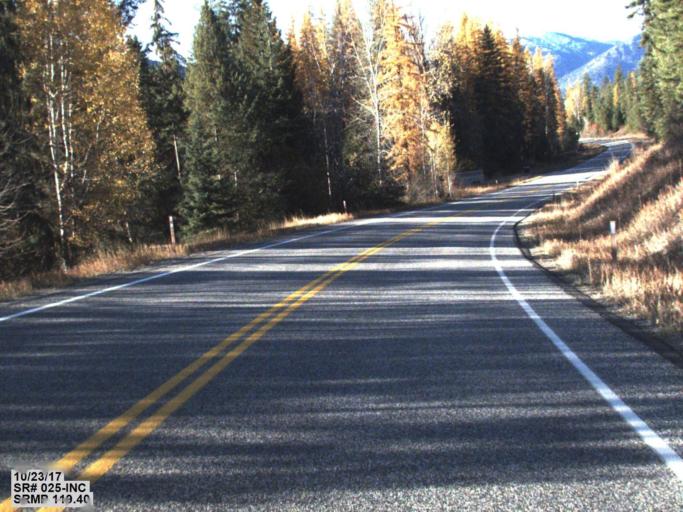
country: CA
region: British Columbia
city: Rossland
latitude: 48.9760
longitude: -117.8203
